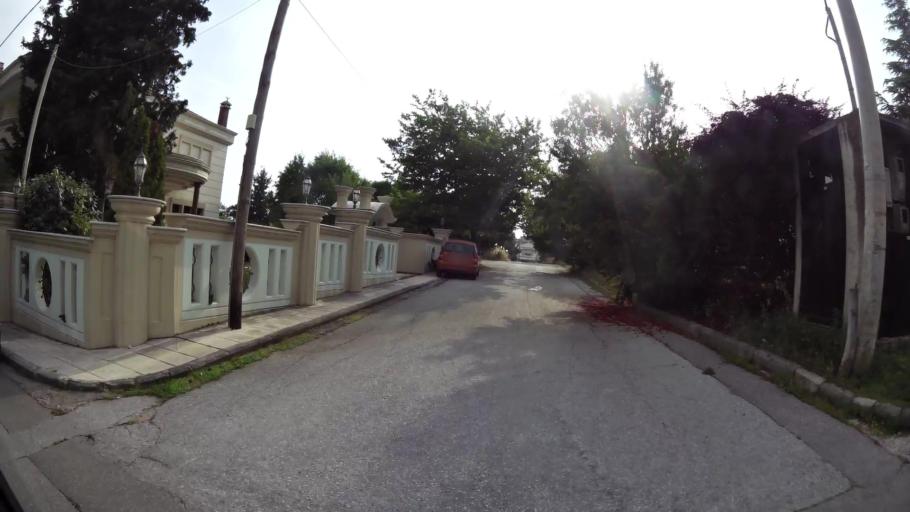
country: GR
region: Central Macedonia
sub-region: Nomos Thessalonikis
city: Oraiokastro
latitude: 40.7278
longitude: 22.9205
